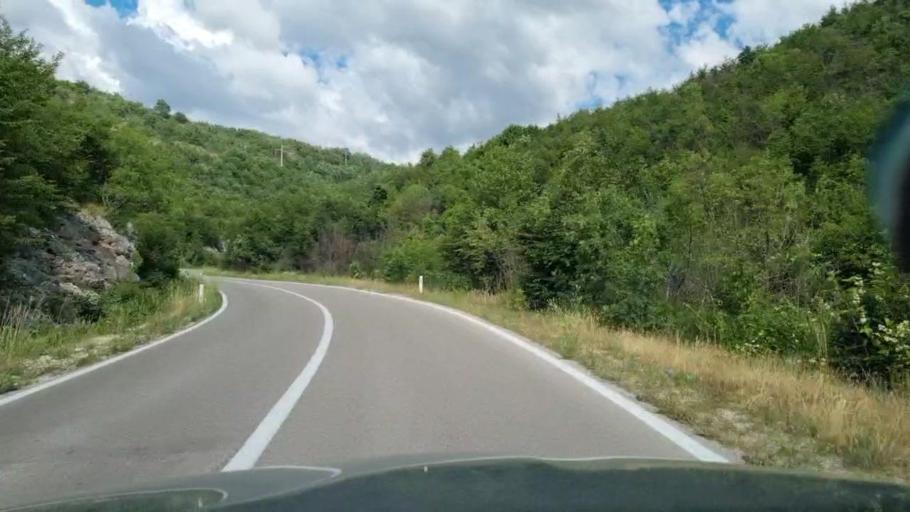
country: BA
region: Republika Srpska
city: Nevesinje
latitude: 43.2643
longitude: 18.0208
